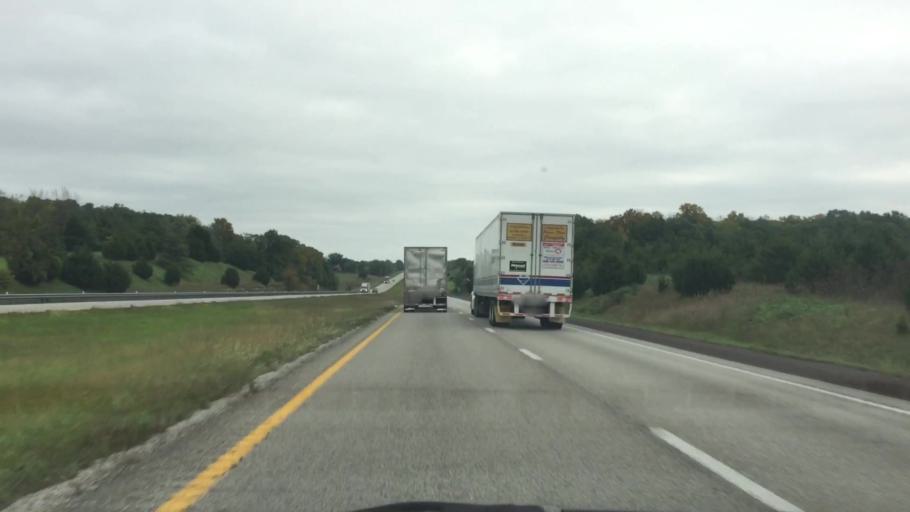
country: US
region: Missouri
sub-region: Clinton County
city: Cameron
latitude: 39.8745
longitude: -94.1666
